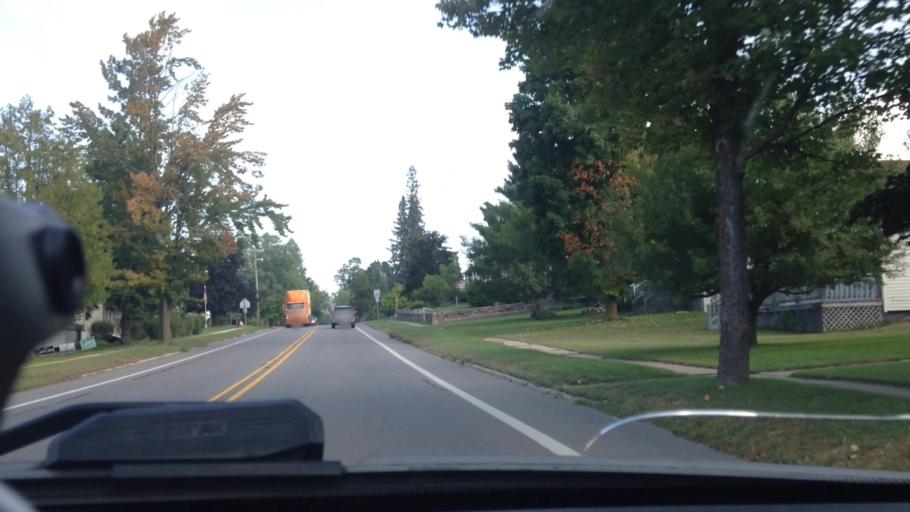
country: US
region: Michigan
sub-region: Dickinson County
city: Norway
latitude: 45.7826
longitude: -87.9098
